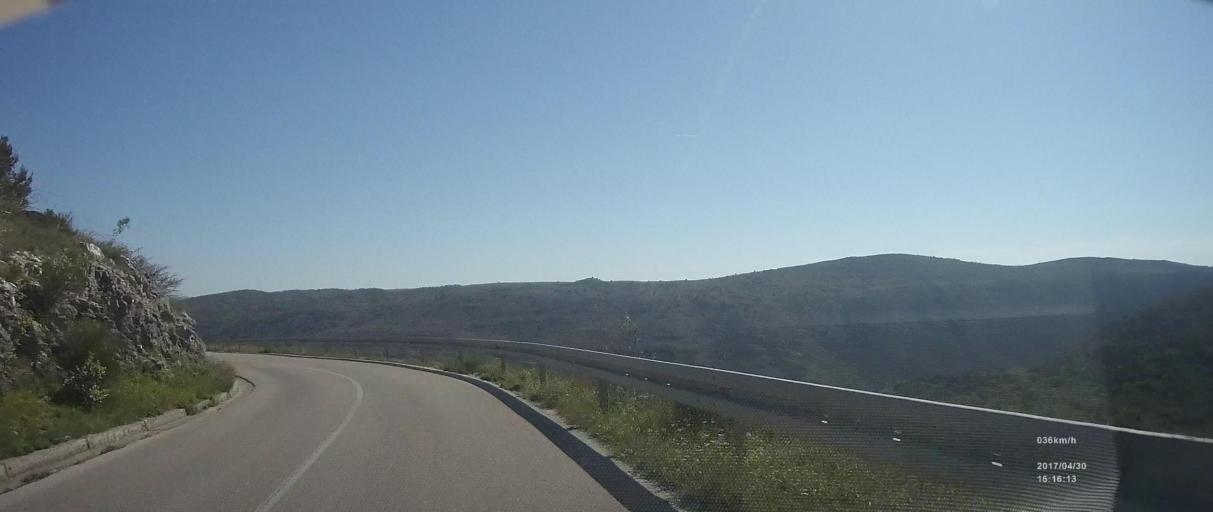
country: HR
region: Splitsko-Dalmatinska
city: Srinjine
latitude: 43.5041
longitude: 16.6055
